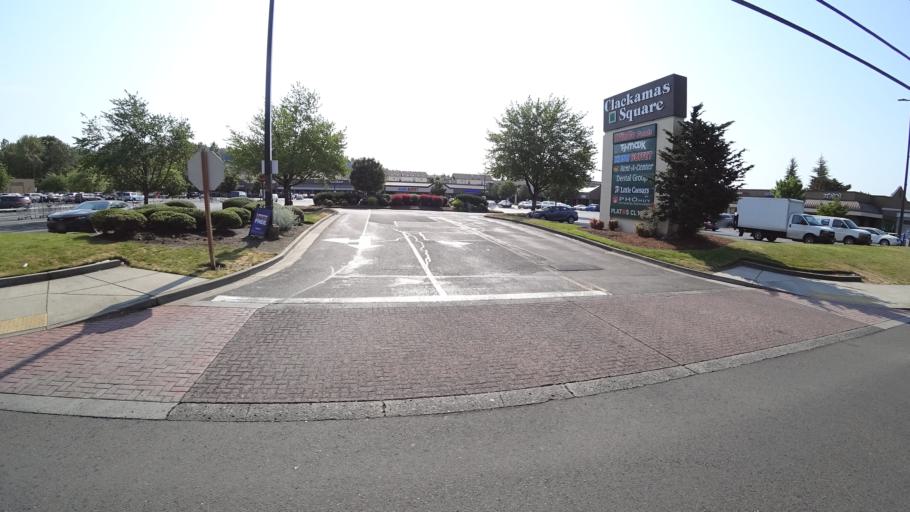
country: US
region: Oregon
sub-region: Clackamas County
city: Oatfield
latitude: 45.4422
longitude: -122.5788
